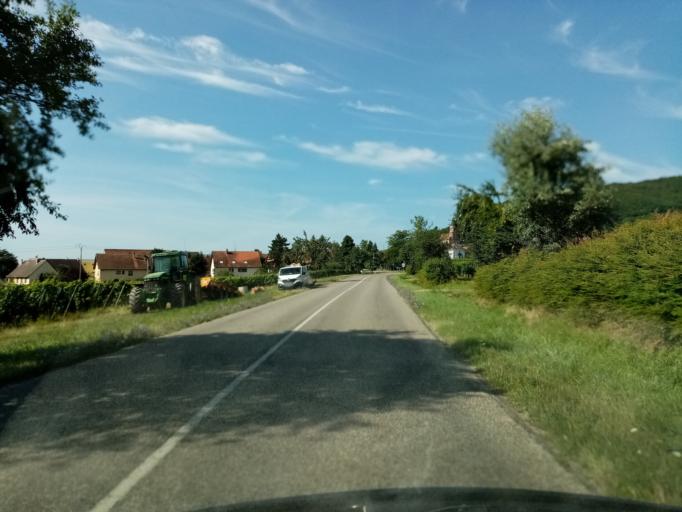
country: FR
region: Alsace
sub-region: Departement du Bas-Rhin
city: Kintzheim
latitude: 48.2448
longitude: 7.3867
